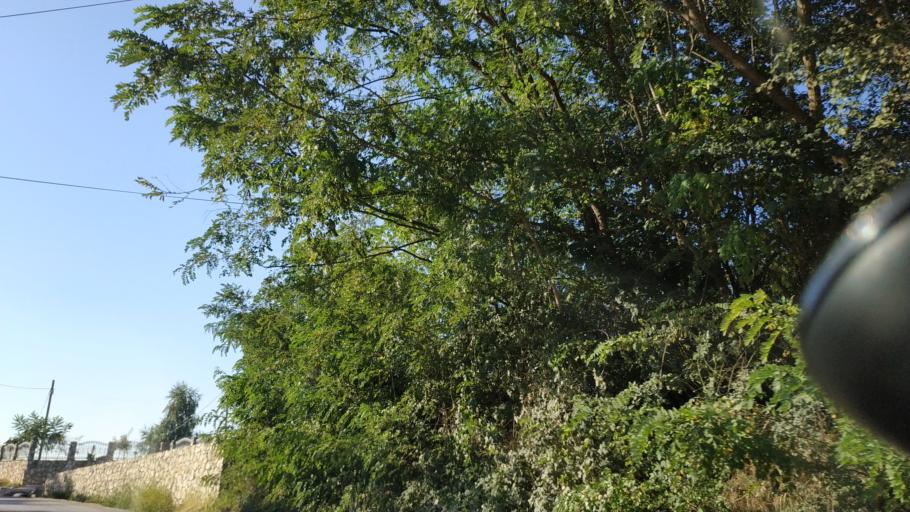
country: RS
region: Central Serbia
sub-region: Rasinski Okrug
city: Krusevac
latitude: 43.5026
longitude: 21.3399
